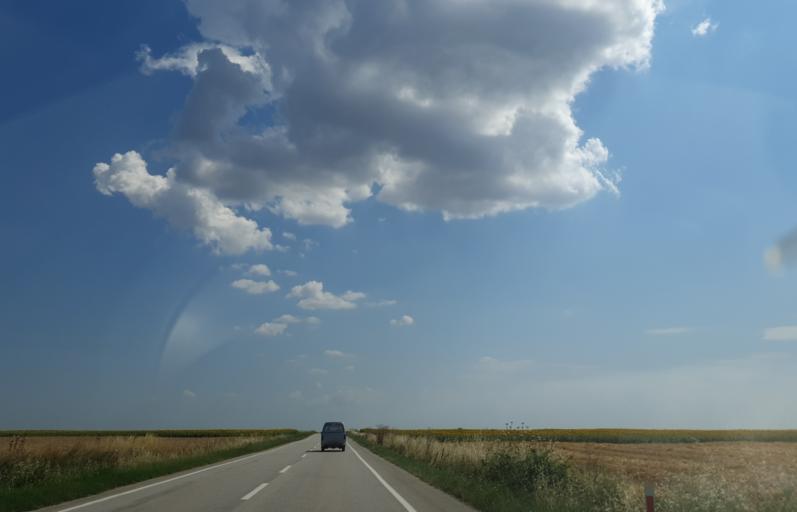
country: TR
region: Kirklareli
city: Buyukkaristiran
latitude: 41.4081
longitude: 27.5765
